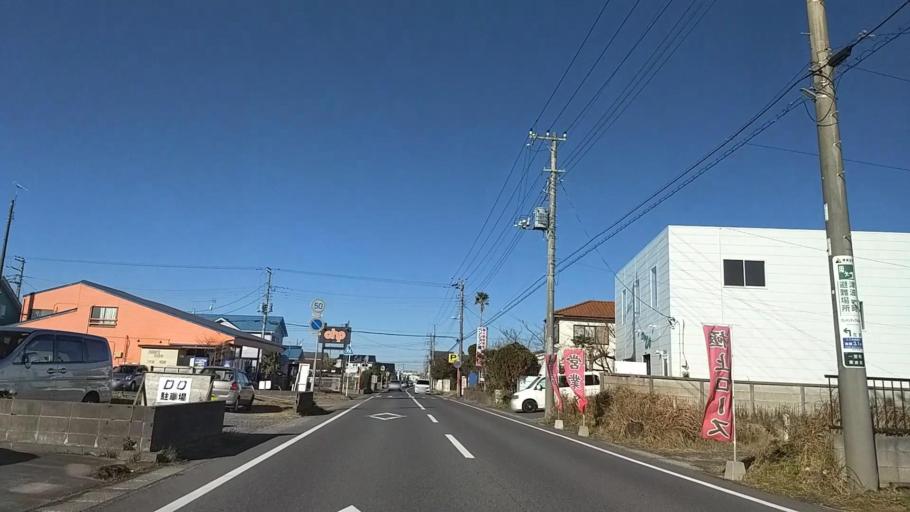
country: JP
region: Chiba
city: Ohara
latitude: 35.3541
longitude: 140.3891
